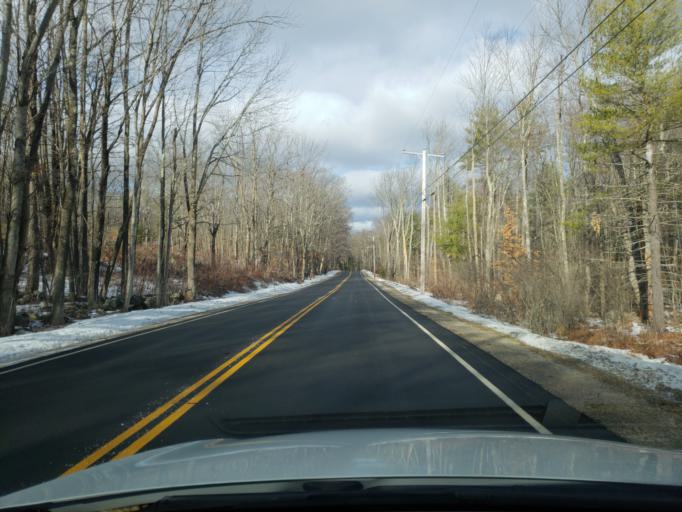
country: US
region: New Hampshire
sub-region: Hillsborough County
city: Greenfield
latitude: 43.0038
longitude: -71.8332
